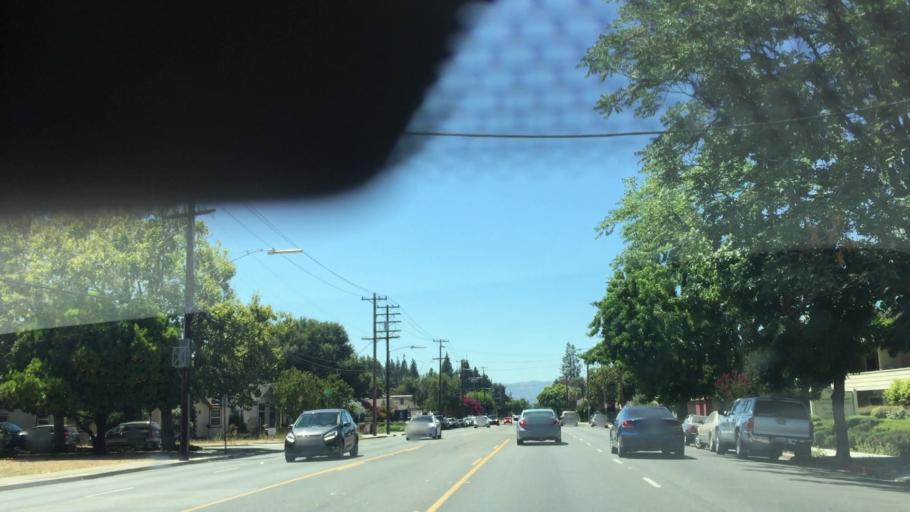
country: US
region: California
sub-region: Santa Clara County
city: Buena Vista
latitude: 37.2945
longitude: -121.9153
